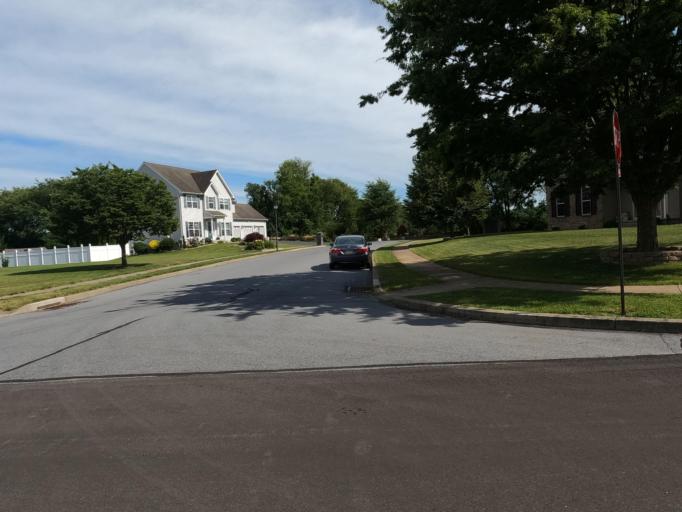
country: US
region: Pennsylvania
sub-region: Lebanon County
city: Campbelltown
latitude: 40.2763
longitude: -76.5957
